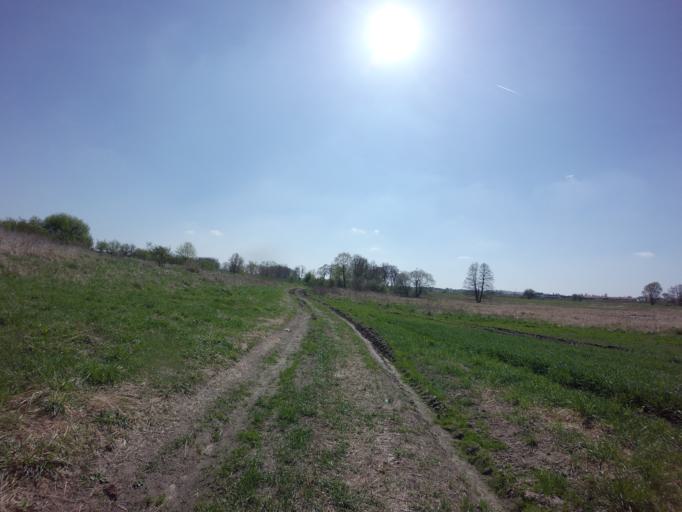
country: PL
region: West Pomeranian Voivodeship
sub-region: Powiat choszczenski
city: Choszczno
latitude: 53.1577
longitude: 15.4558
